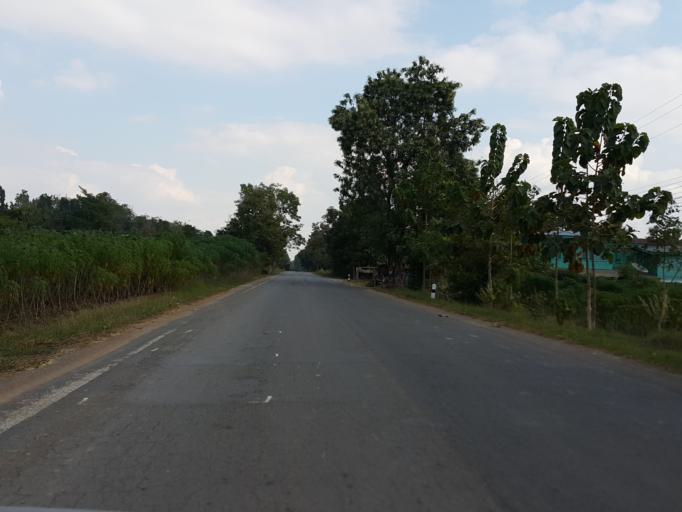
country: TH
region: Sukhothai
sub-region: Amphoe Si Satchanalai
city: Si Satchanalai
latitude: 17.4586
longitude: 99.6702
